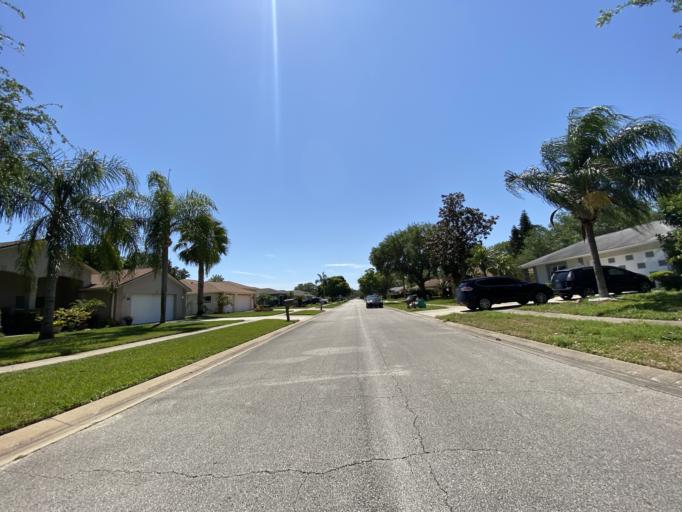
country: US
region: Florida
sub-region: Volusia County
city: South Daytona
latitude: 29.1541
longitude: -81.0074
